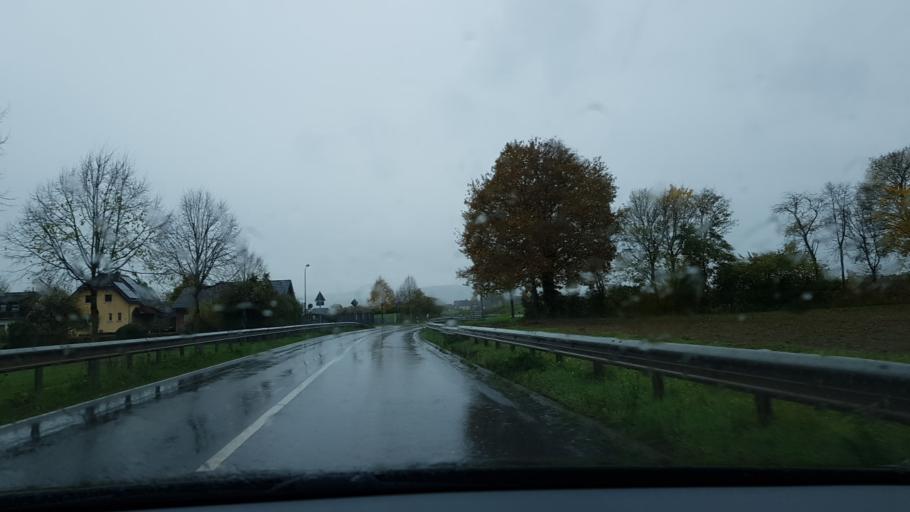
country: DE
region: Rheinland-Pfalz
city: Neuerburg
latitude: 49.9825
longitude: 6.9377
